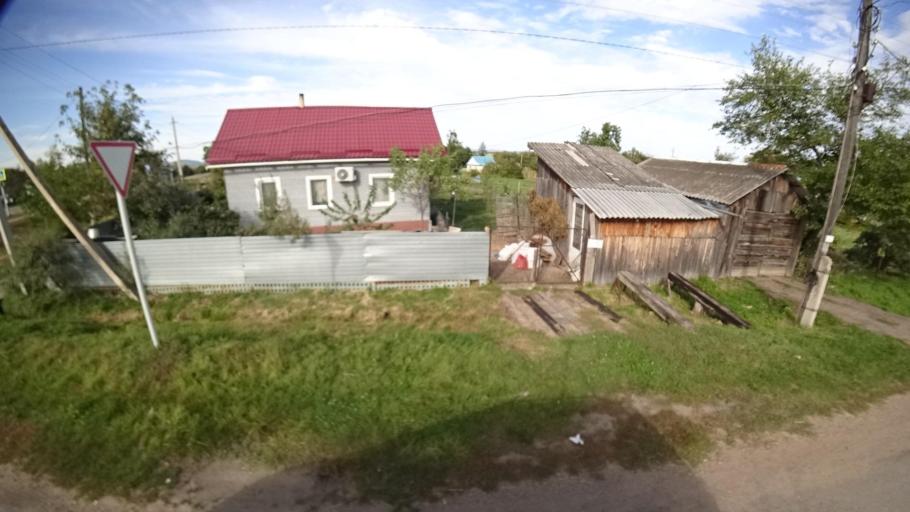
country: RU
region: Primorskiy
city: Dostoyevka
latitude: 44.3008
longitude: 133.4493
